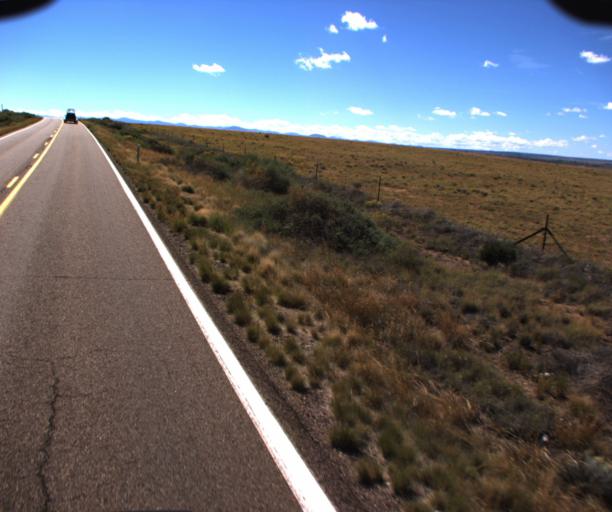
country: US
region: Arizona
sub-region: Apache County
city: Saint Johns
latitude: 34.5621
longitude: -109.3412
